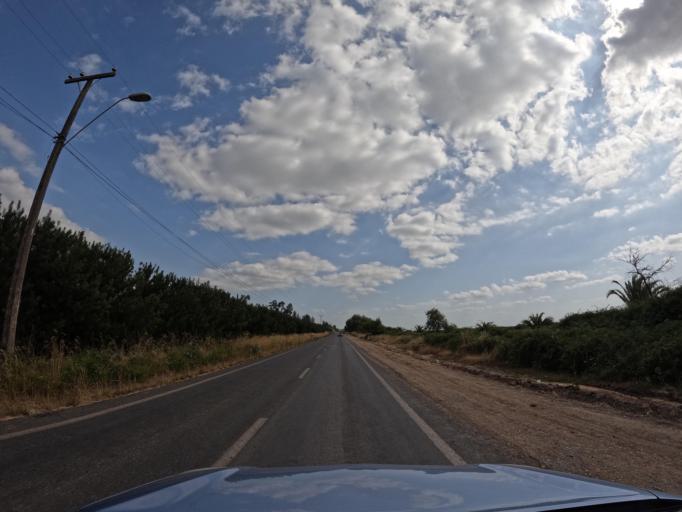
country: CL
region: Maule
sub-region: Provincia de Curico
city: Molina
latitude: -35.1845
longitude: -71.2951
